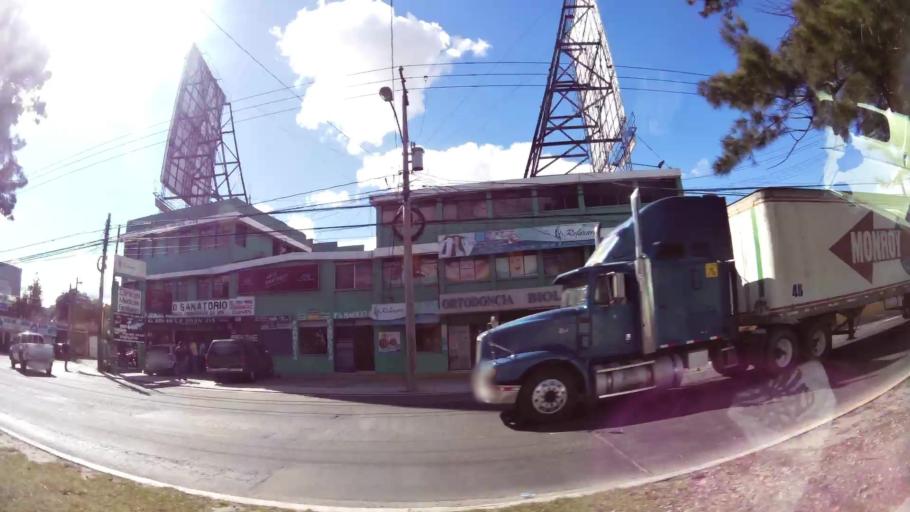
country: GT
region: Guatemala
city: Santa Catarina Pinula
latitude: 14.5924
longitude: -90.5447
